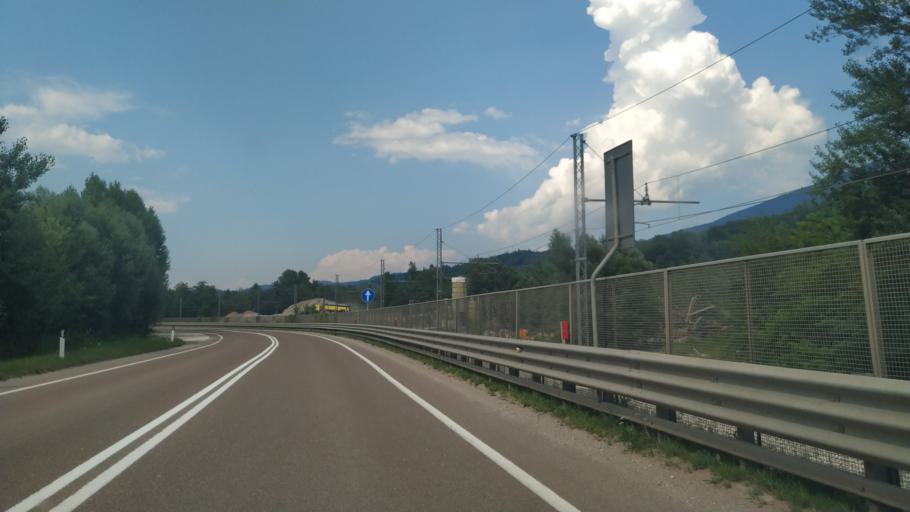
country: IT
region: Trentino-Alto Adige
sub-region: Provincia di Trento
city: Campodenno
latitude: 46.2486
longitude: 11.0578
